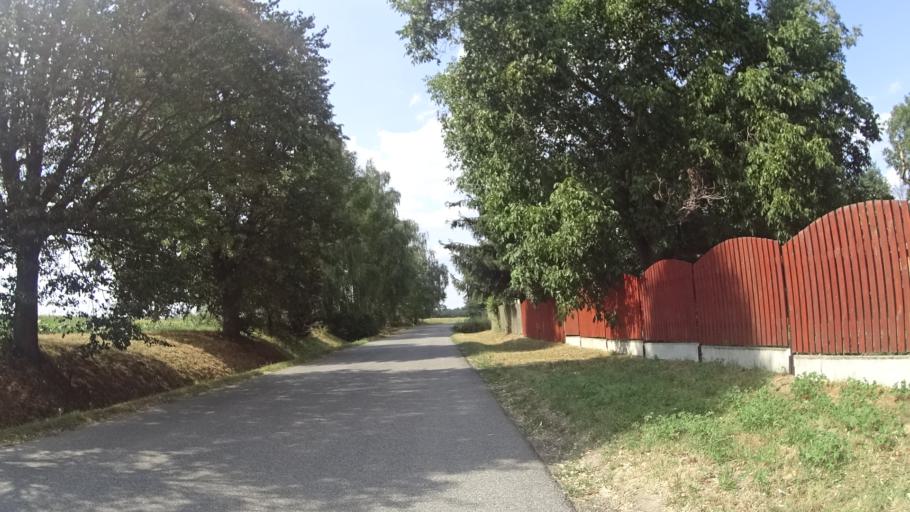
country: CZ
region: Kralovehradecky
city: Liban
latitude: 50.4084
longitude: 15.2663
